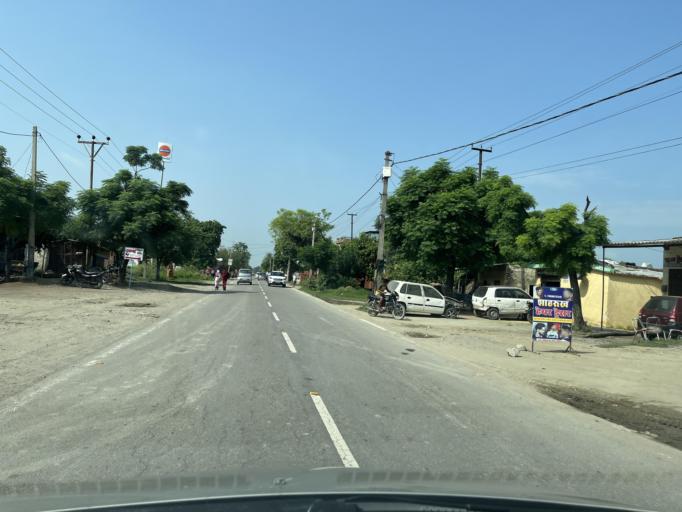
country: IN
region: Uttarakhand
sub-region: Udham Singh Nagar
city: Bazpur
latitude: 29.2084
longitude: 79.2133
